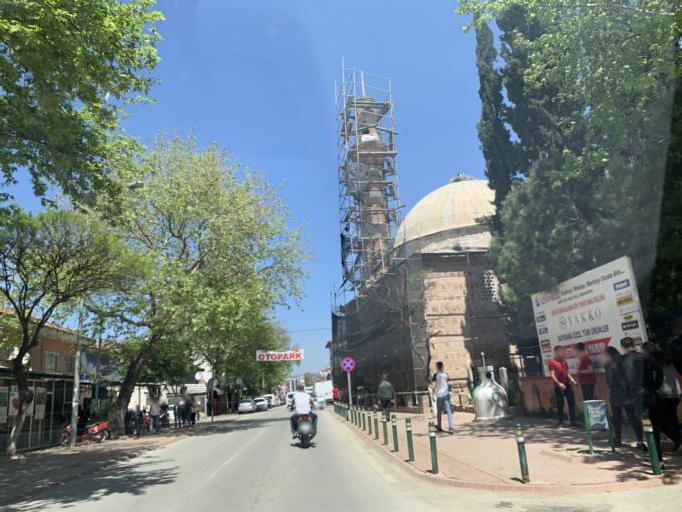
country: TR
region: Bursa
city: Iznik
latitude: 40.4277
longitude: 29.7196
